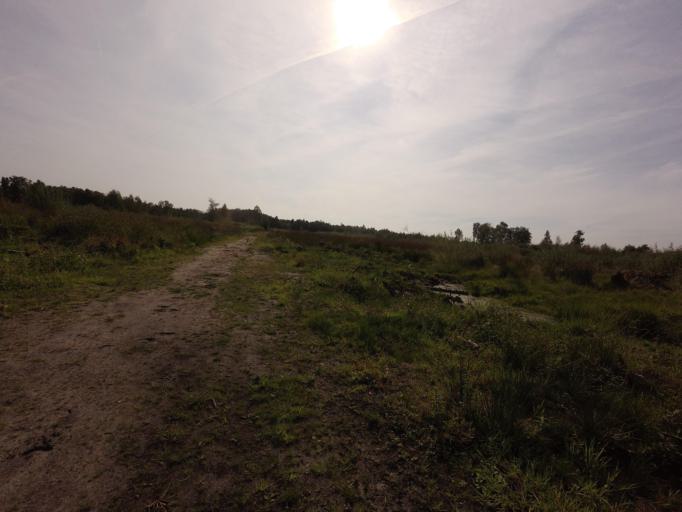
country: NL
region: Overijssel
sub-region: Gemeente Enschede
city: Enschede
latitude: 52.1889
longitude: 6.9541
